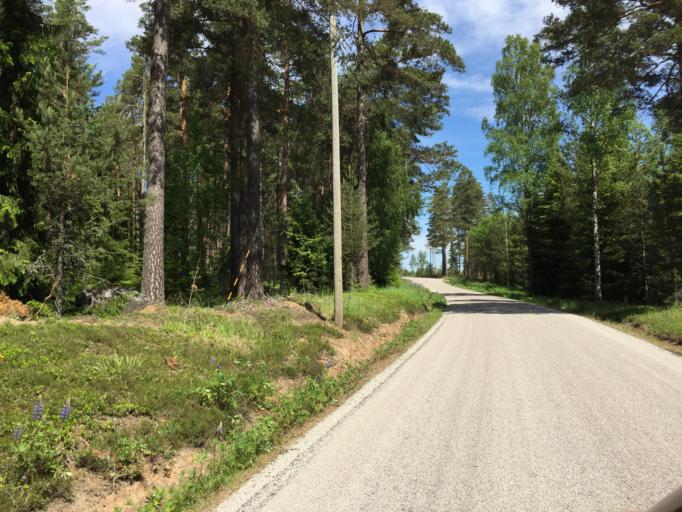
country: SE
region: Soedermanland
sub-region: Vingakers Kommun
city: Vingaker
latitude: 58.9532
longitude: 15.6698
